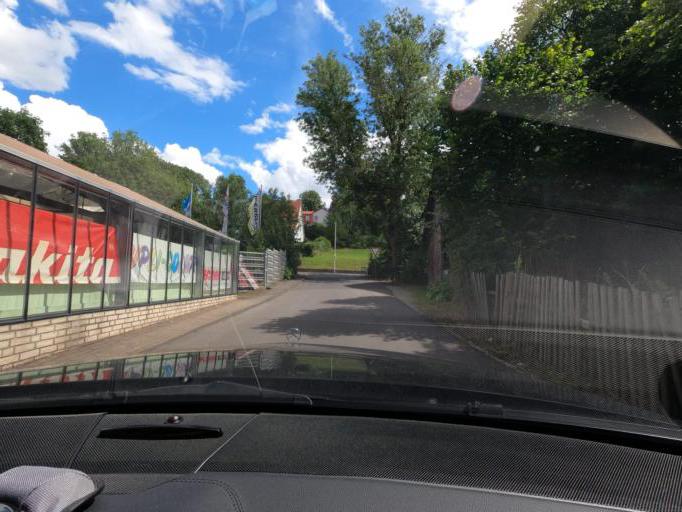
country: DE
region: Hesse
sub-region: Regierungsbezirk Kassel
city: Sontra
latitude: 51.0666
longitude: 9.9303
